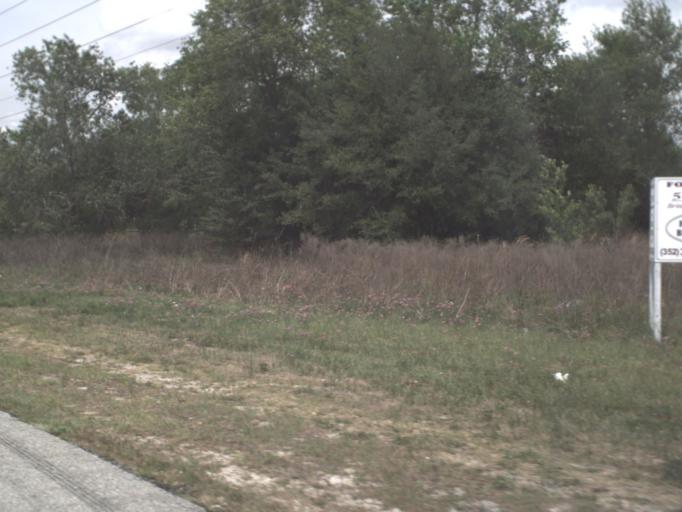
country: US
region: Florida
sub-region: Lake County
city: Mount Plymouth
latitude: 28.8513
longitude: -81.5861
